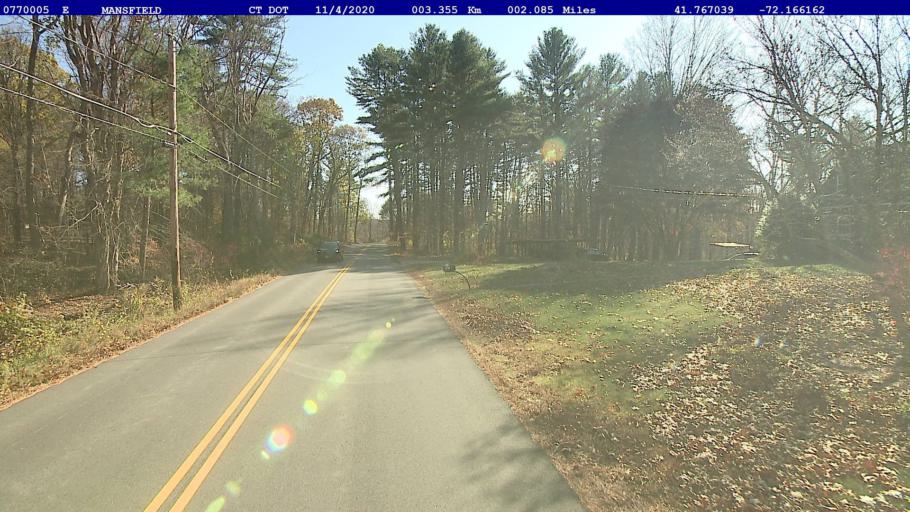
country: US
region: Connecticut
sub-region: Tolland County
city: Mansfield City
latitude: 41.7670
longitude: -72.1662
